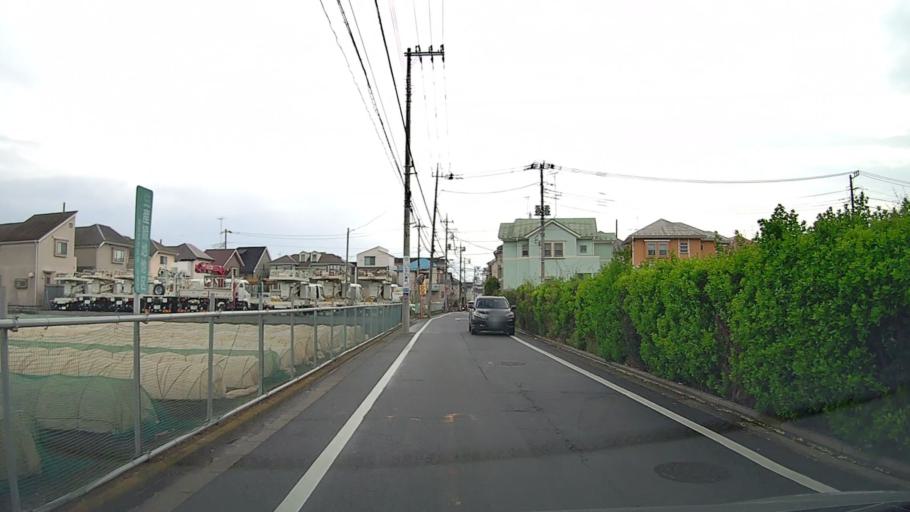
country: JP
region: Tokyo
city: Musashino
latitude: 35.7407
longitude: 139.5814
